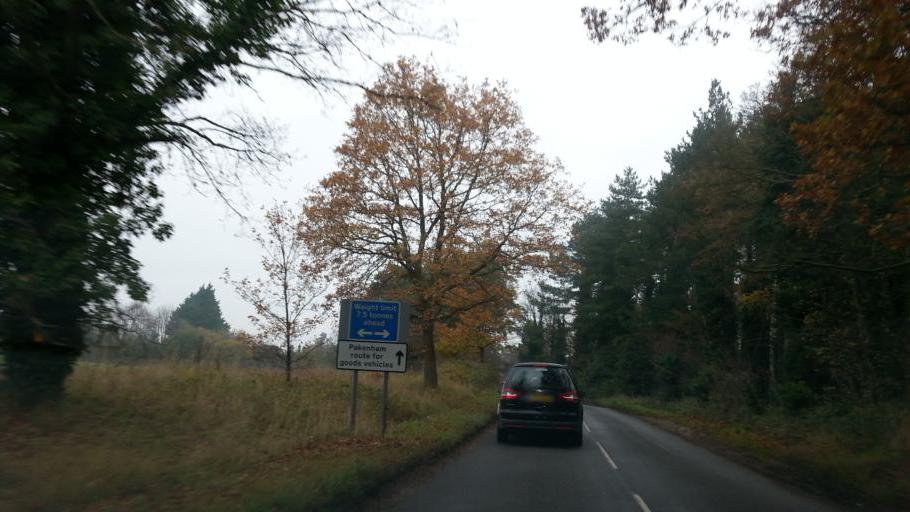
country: GB
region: England
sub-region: Suffolk
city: Thurston
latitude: 52.2486
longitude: 0.8075
